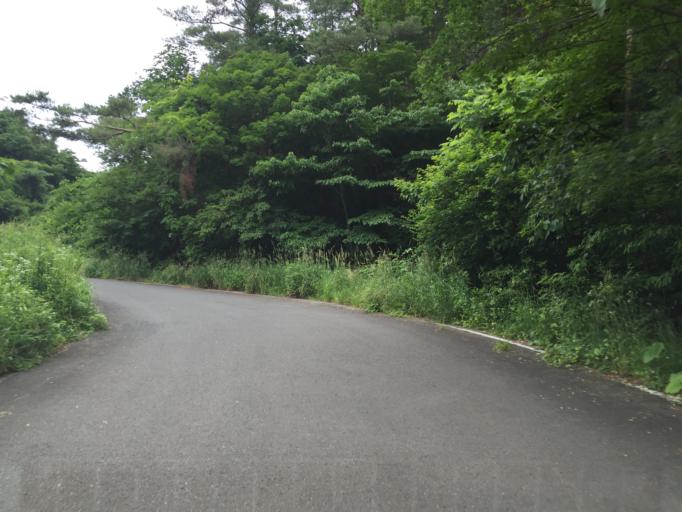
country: JP
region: Fukushima
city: Yanagawamachi-saiwaicho
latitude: 37.7947
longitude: 140.7071
